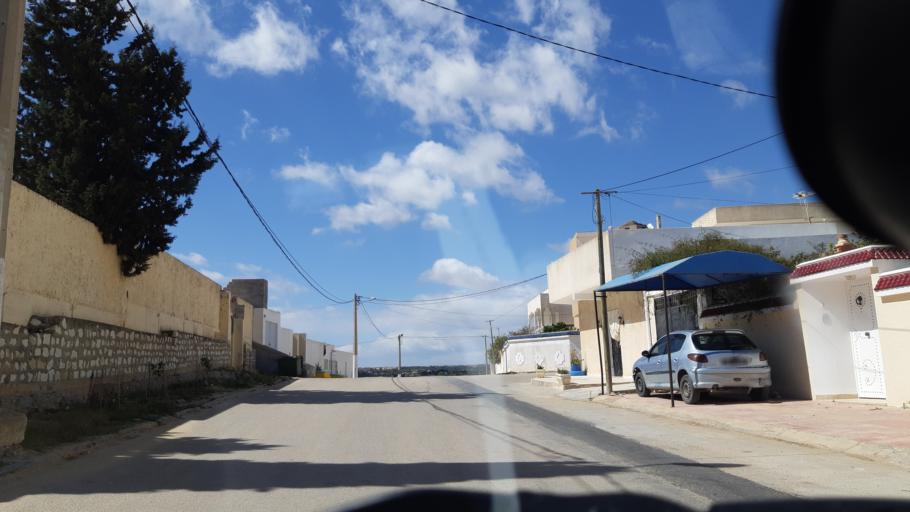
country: TN
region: Susah
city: Akouda
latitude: 35.8907
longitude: 10.5337
